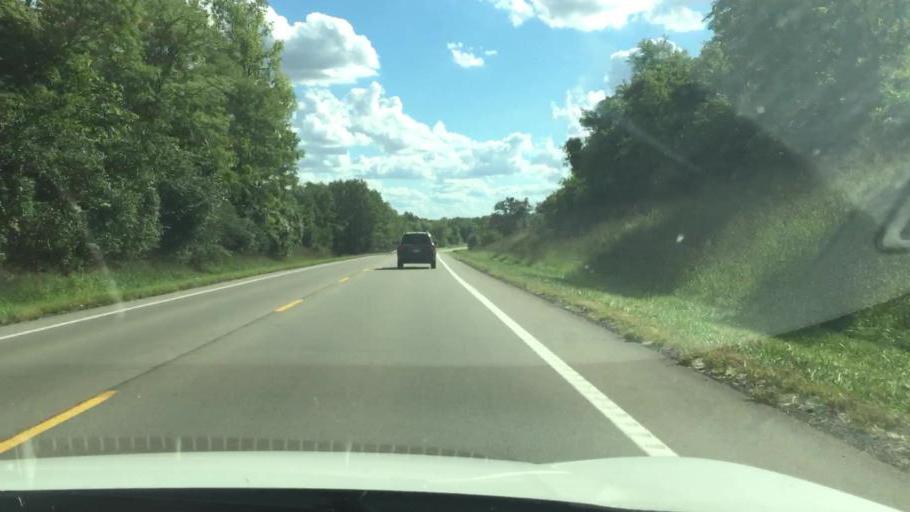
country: US
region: Ohio
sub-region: Clark County
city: Northridge
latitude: 39.9896
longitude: -83.7312
